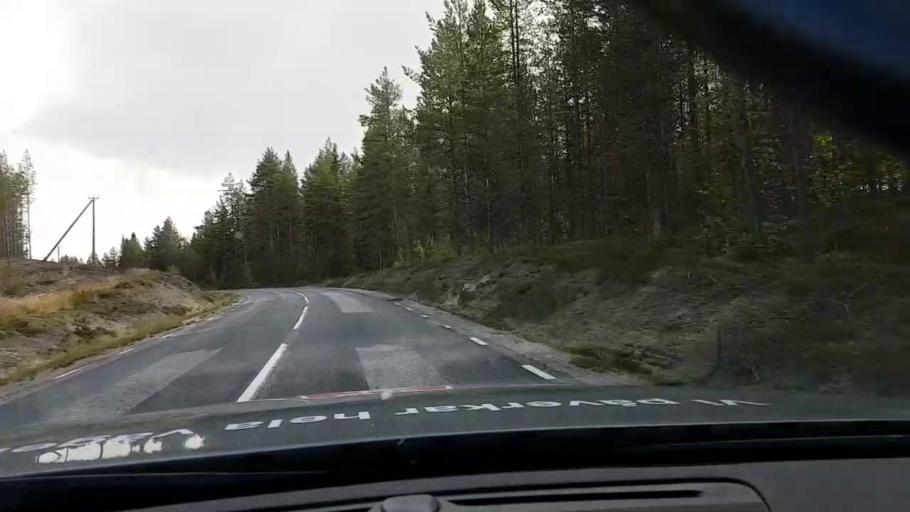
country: SE
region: Vaesterbotten
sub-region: Asele Kommun
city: Asele
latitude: 63.8513
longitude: 17.3946
